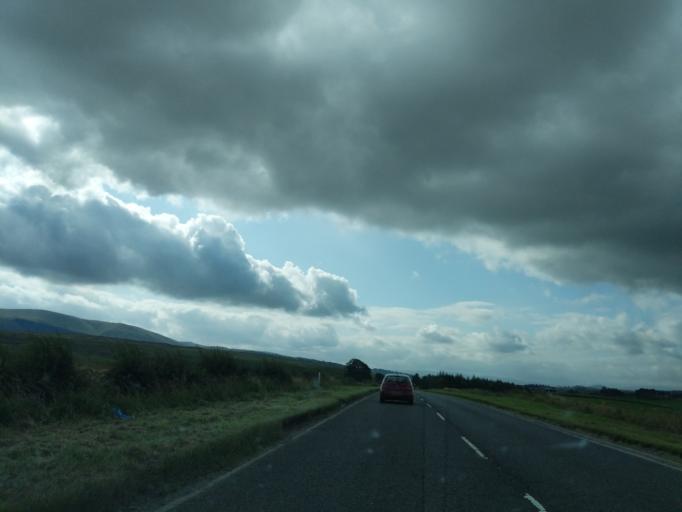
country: GB
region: Scotland
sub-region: Midlothian
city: Penicuik
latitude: 55.7633
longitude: -3.2077
